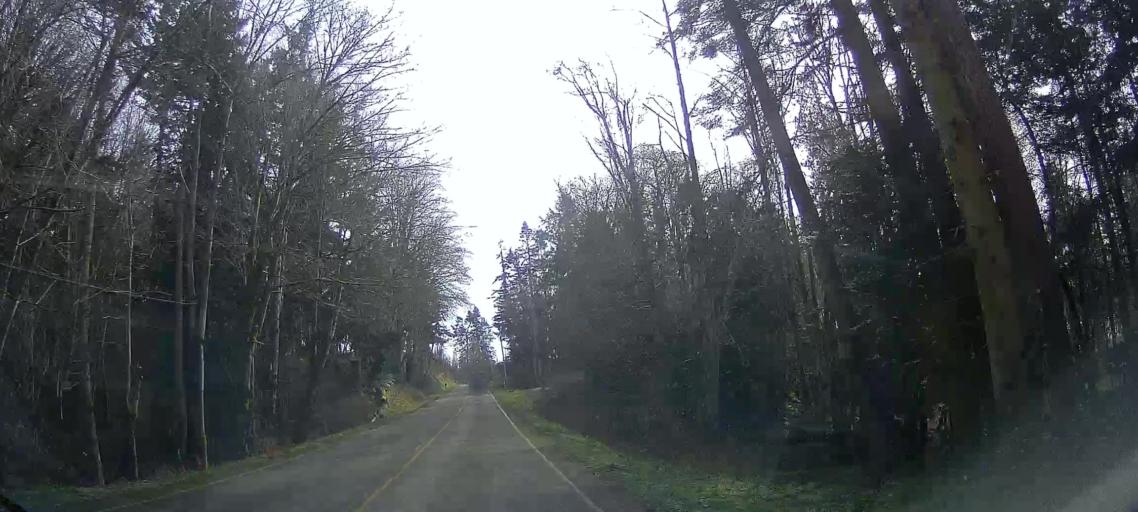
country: US
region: Washington
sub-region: Island County
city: Langley
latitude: 48.0756
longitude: -122.3891
